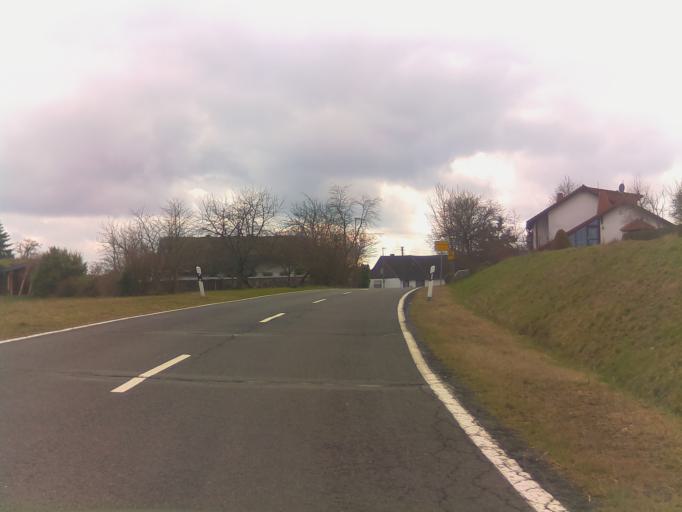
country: DE
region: Rheinland-Pfalz
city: Oberhambach
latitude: 49.6762
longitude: 7.1616
